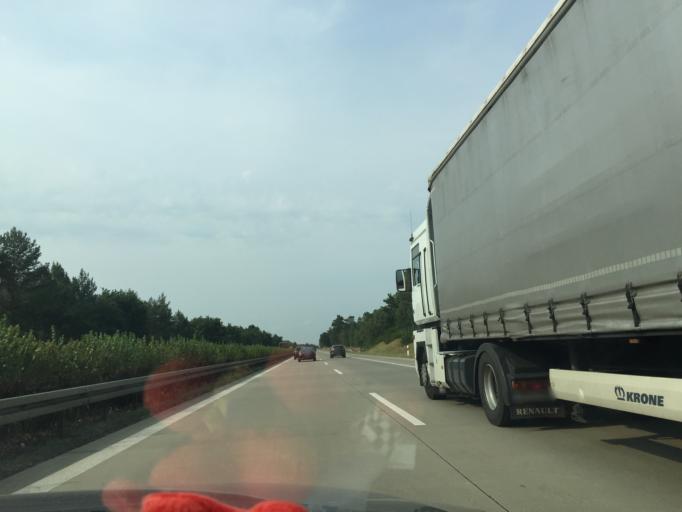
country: DE
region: Brandenburg
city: Teupitz
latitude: 52.0713
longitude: 13.6512
